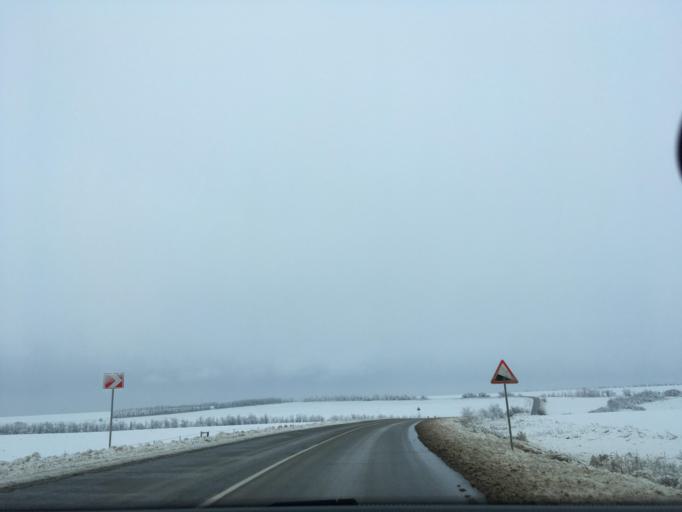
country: RU
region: Voronezj
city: Ol'khovatka
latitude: 50.2181
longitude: 39.2603
